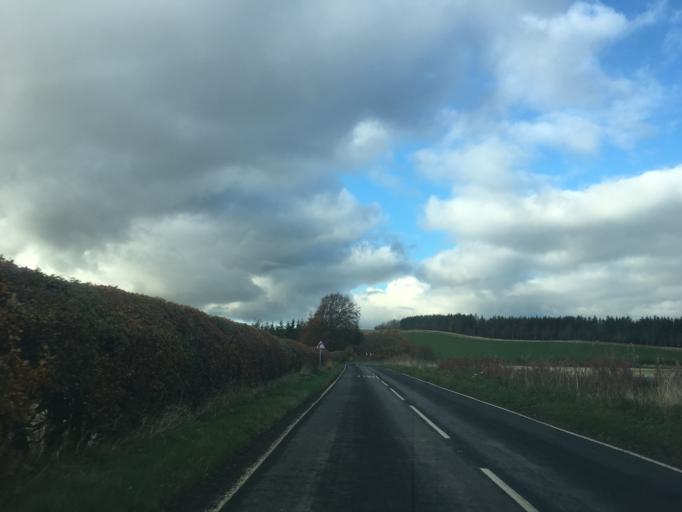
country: GB
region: Scotland
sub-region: East Lothian
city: Pencaitland
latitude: 55.8474
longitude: -2.8748
